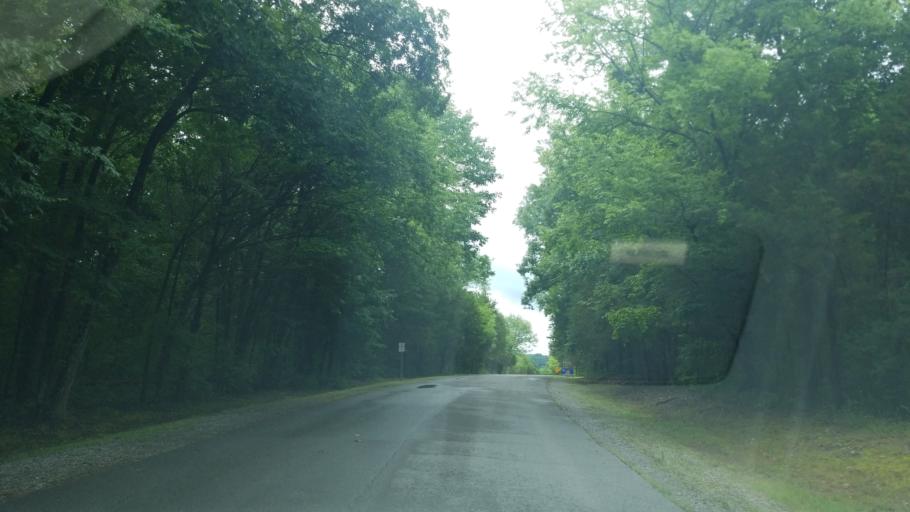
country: US
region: Tennessee
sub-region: Rutherford County
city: La Vergne
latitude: 36.1081
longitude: -86.5993
